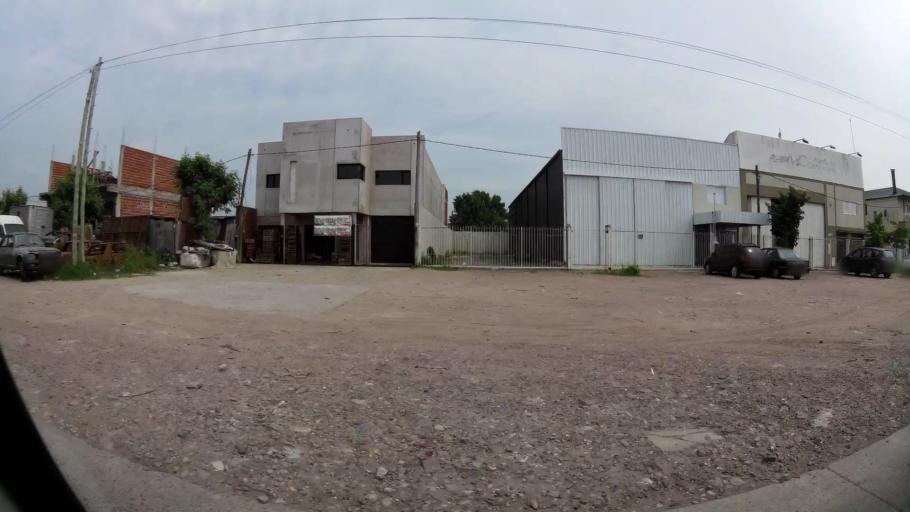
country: AR
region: Buenos Aires
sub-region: Partido de La Plata
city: La Plata
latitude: -34.9039
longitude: -57.9975
